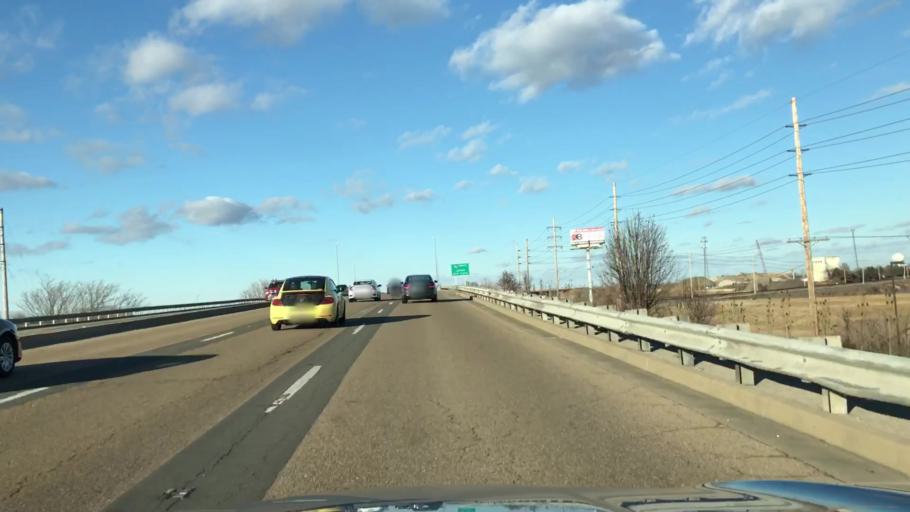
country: US
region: Illinois
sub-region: McLean County
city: Normal
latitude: 40.5275
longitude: -88.9518
